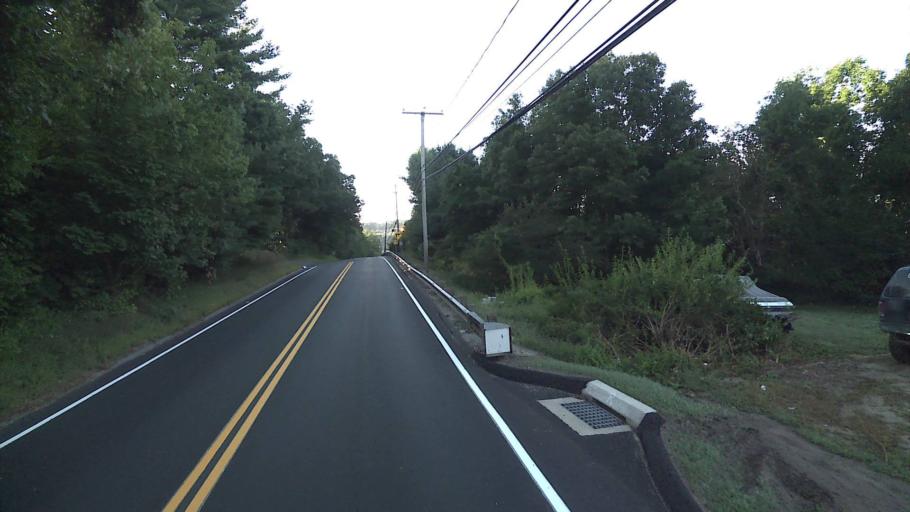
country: US
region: Connecticut
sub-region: Tolland County
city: Tolland
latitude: 41.8598
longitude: -72.3008
